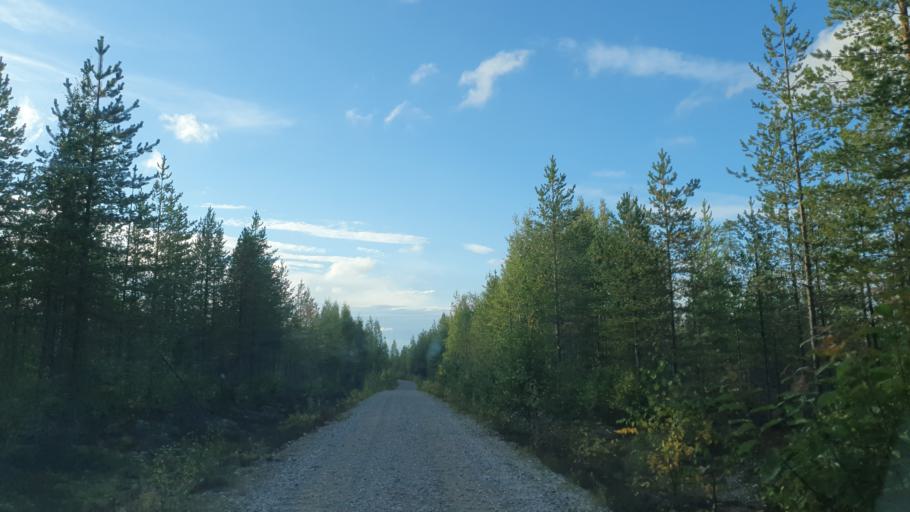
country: FI
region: Kainuu
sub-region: Kehys-Kainuu
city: Kuhmo
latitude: 64.3334
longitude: 30.0104
